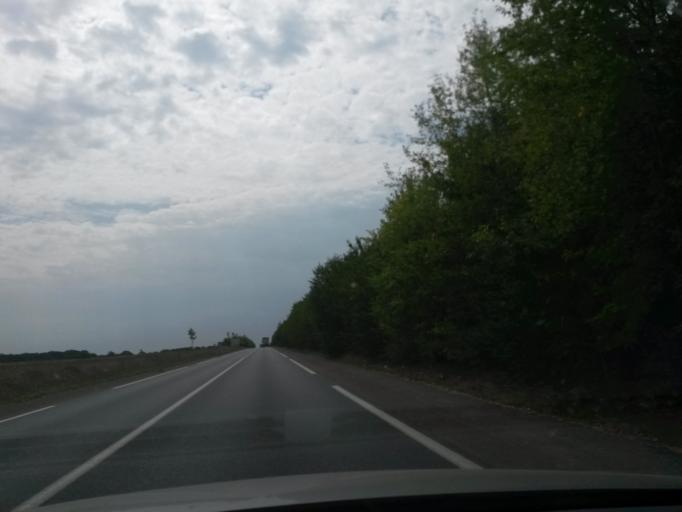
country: FR
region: Poitou-Charentes
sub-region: Departement de la Charente-Maritime
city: Saint-Xandre
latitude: 46.1945
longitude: -1.0951
